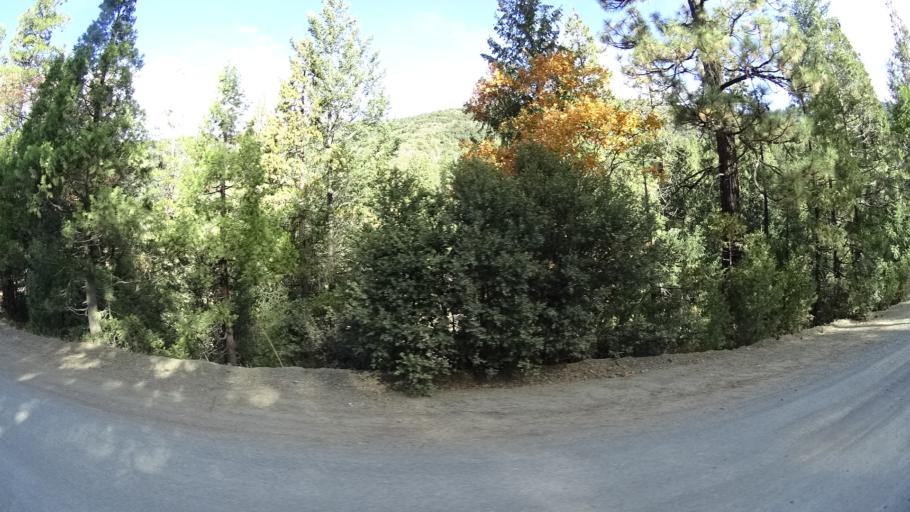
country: US
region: California
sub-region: Siskiyou County
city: Yreka
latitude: 41.7171
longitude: -122.7739
